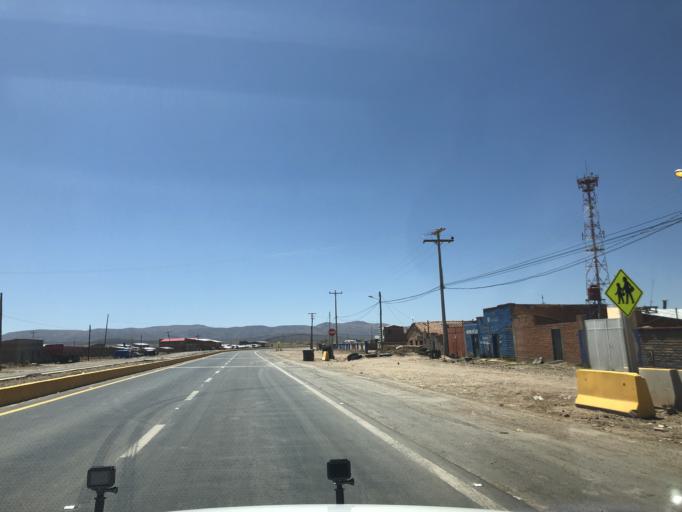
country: BO
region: La Paz
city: Colquiri
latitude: -17.6497
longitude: -67.2068
